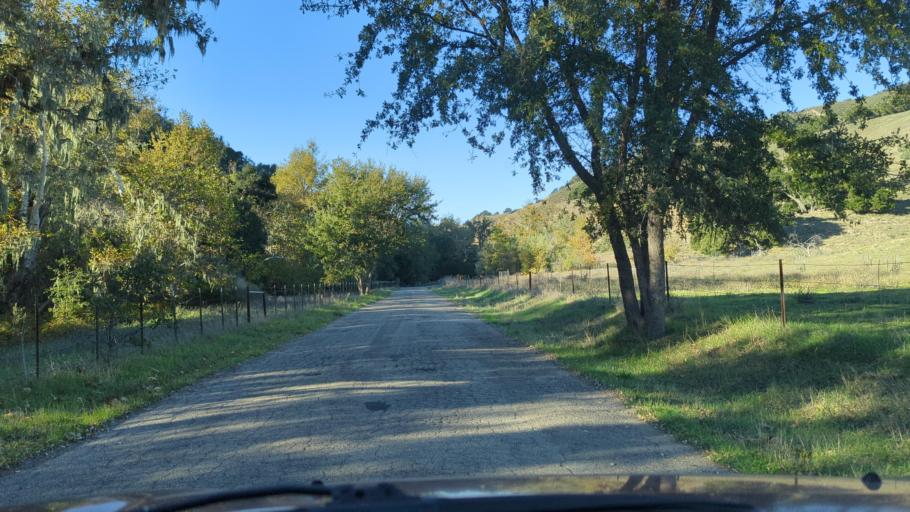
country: US
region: California
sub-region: Santa Barbara County
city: Santa Ynez
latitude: 34.5567
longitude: -120.0828
